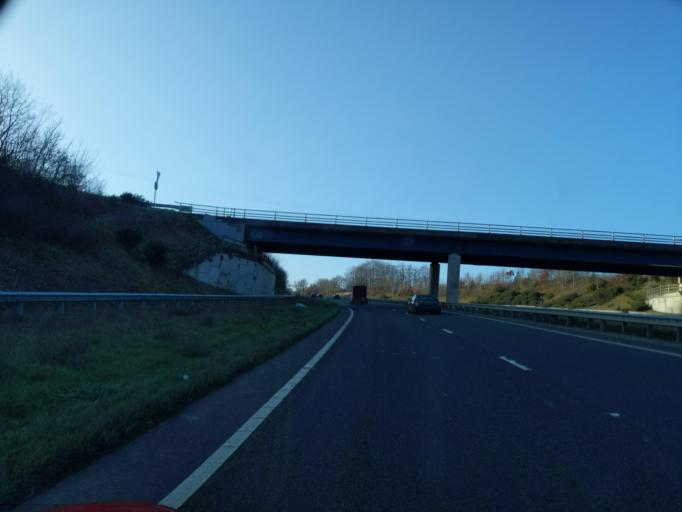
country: GB
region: England
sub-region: Cornwall
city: Liskeard
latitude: 50.4576
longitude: -4.4961
